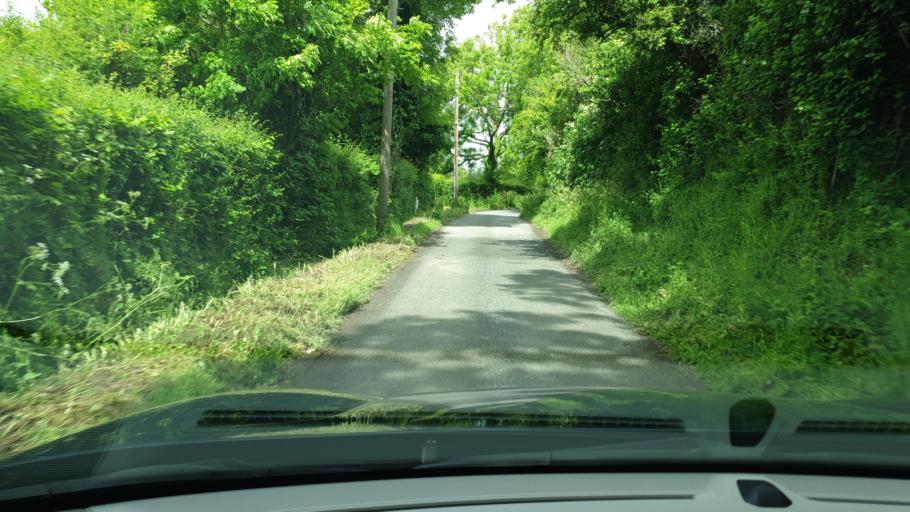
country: IE
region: Leinster
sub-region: Kildare
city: Celbridge
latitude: 53.3701
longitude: -6.5328
